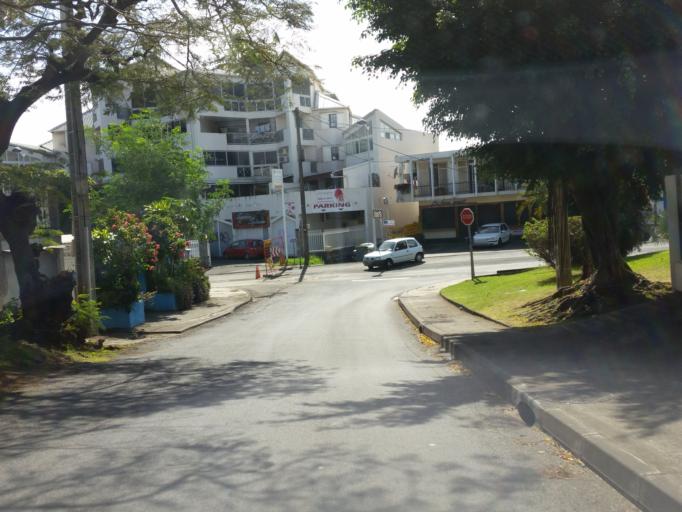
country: RE
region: Reunion
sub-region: Reunion
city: Saint-Denis
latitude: -20.8933
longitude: 55.4662
